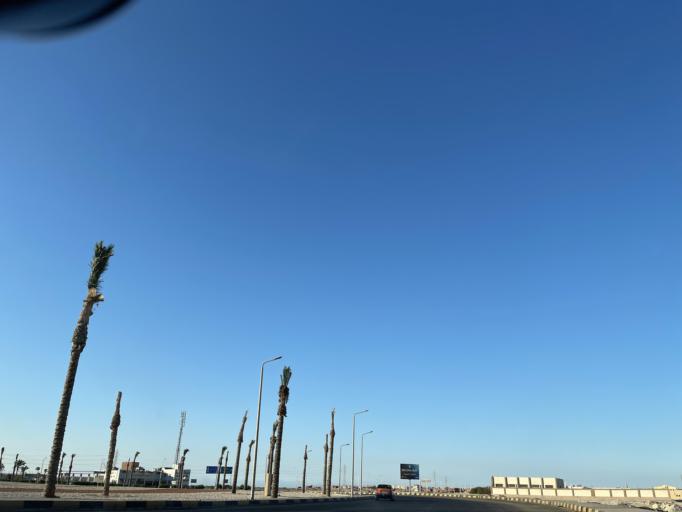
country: EG
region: Red Sea
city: Hurghada
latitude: 27.2304
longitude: 33.7813
